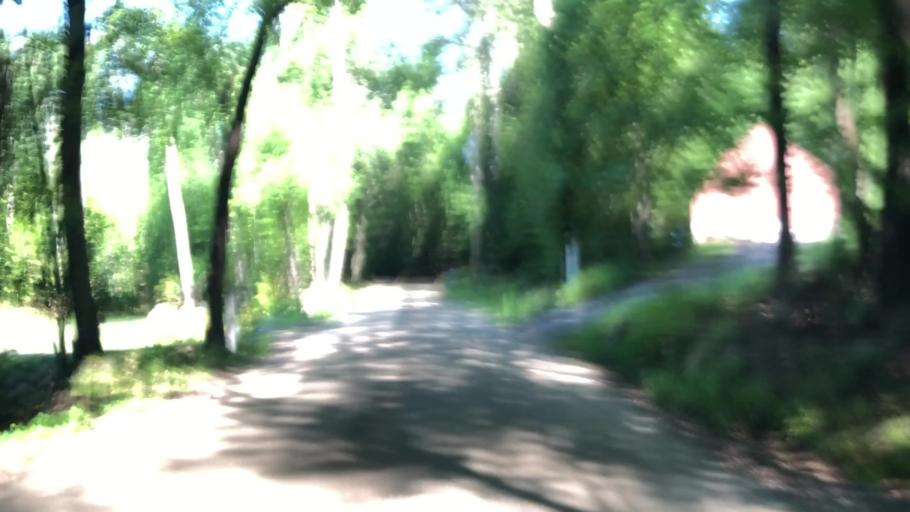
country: US
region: New Hampshire
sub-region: Hillsborough County
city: Mont Vernon
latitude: 42.9154
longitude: -71.6127
